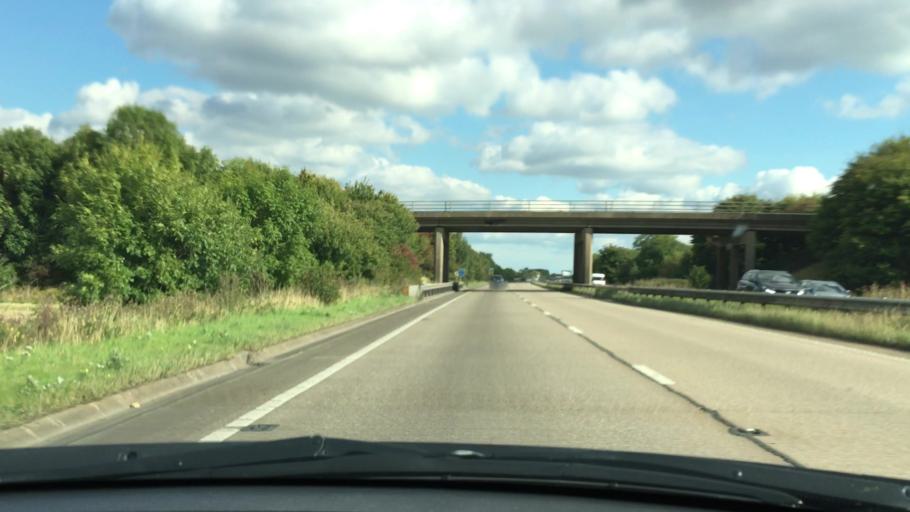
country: GB
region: England
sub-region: North East Lincolnshire
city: Healing
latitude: 53.5944
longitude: -0.1748
